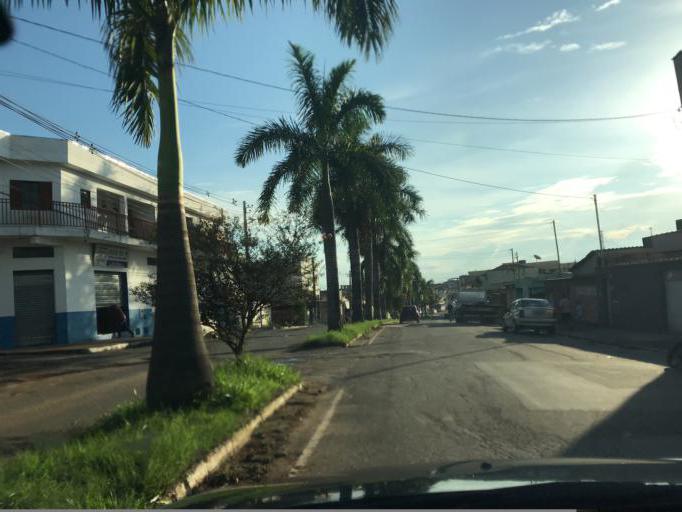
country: BR
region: Minas Gerais
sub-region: Tres Coracoes
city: Tres Coracoes
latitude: -21.6918
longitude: -45.2407
